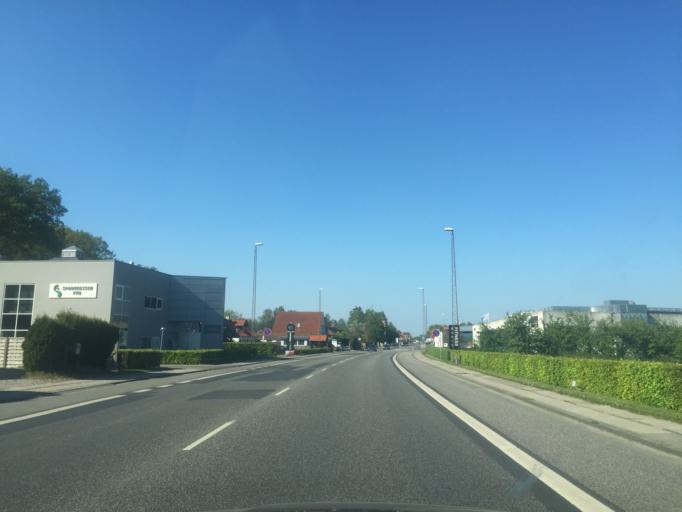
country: DK
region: South Denmark
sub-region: Odense Kommune
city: Odense
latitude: 55.3672
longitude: 10.3924
